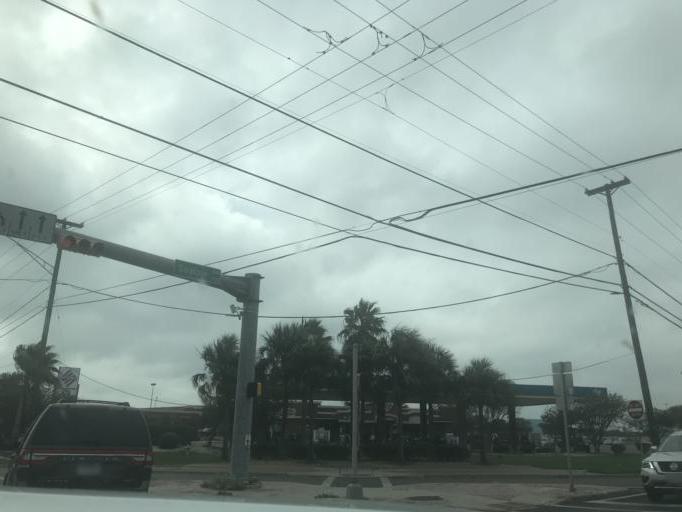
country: US
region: Texas
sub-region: Nueces County
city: Corpus Christi
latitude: 27.6855
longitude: -97.3839
